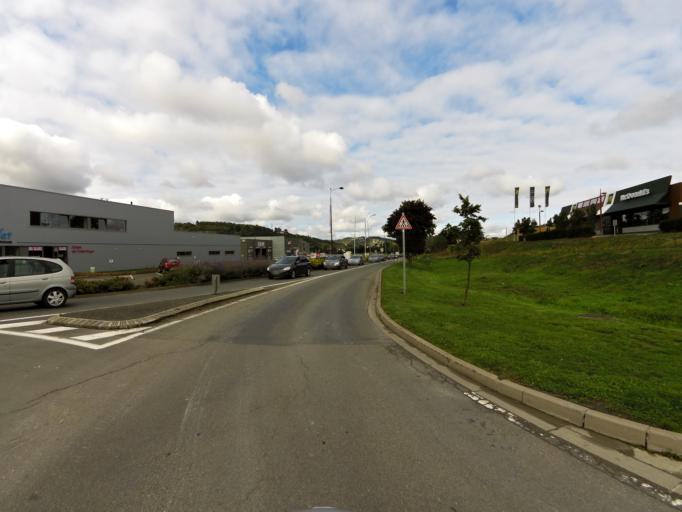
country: FR
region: Champagne-Ardenne
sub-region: Departement des Ardennes
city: Fromelennes
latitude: 50.1337
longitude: 4.8519
